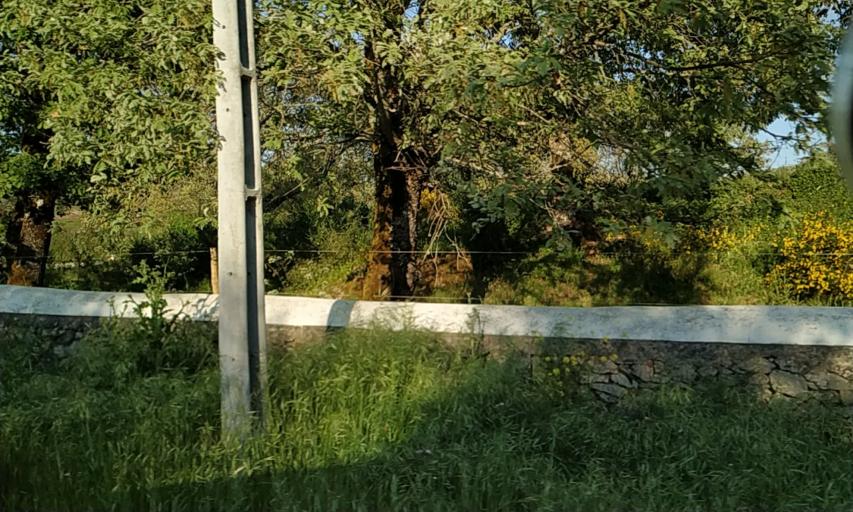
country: PT
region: Portalegre
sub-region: Marvao
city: Marvao
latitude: 39.3498
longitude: -7.4058
